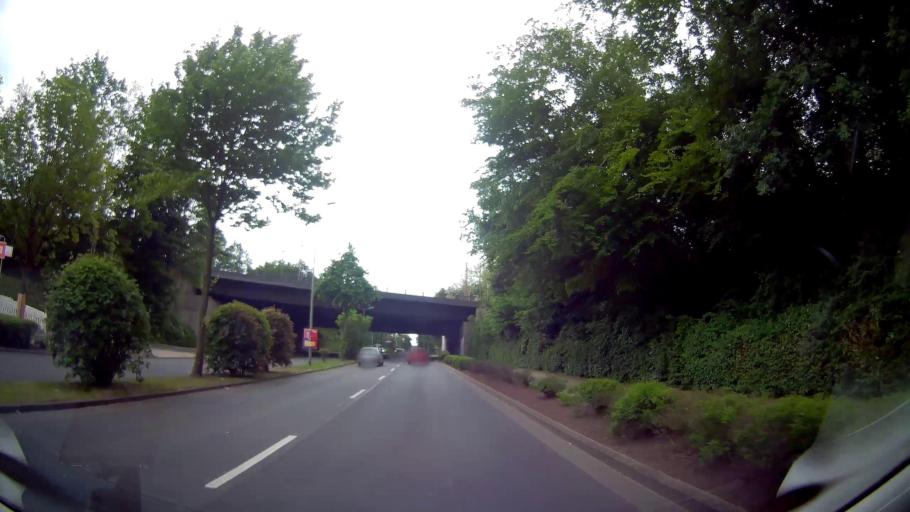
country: DE
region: North Rhine-Westphalia
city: Bochum-Hordel
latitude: 51.5227
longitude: 7.1561
